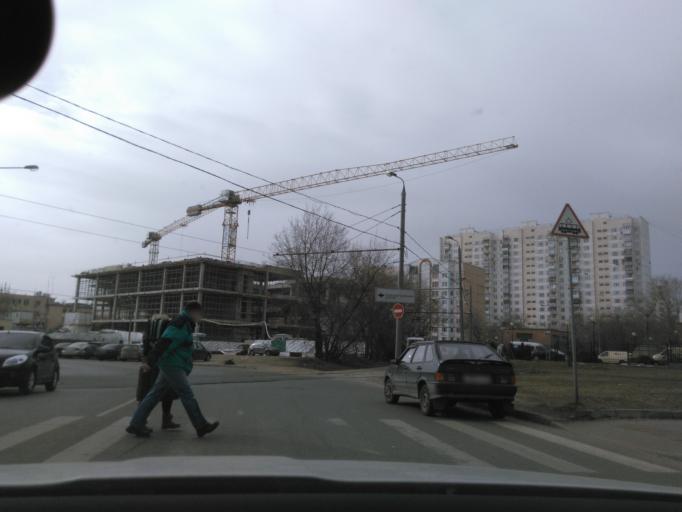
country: RU
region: Moskovskaya
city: Koptevo
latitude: 55.8269
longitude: 37.5170
